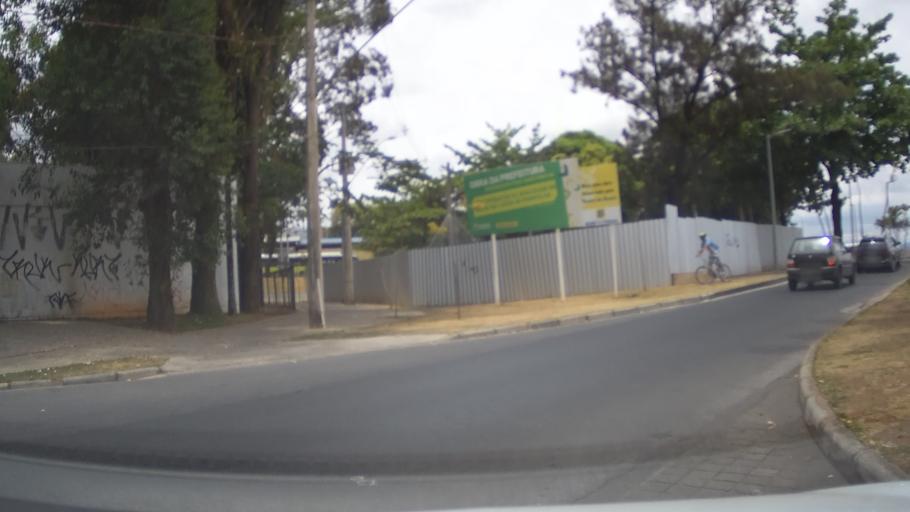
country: BR
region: Minas Gerais
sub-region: Belo Horizonte
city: Belo Horizonte
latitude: -19.8440
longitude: -43.9680
